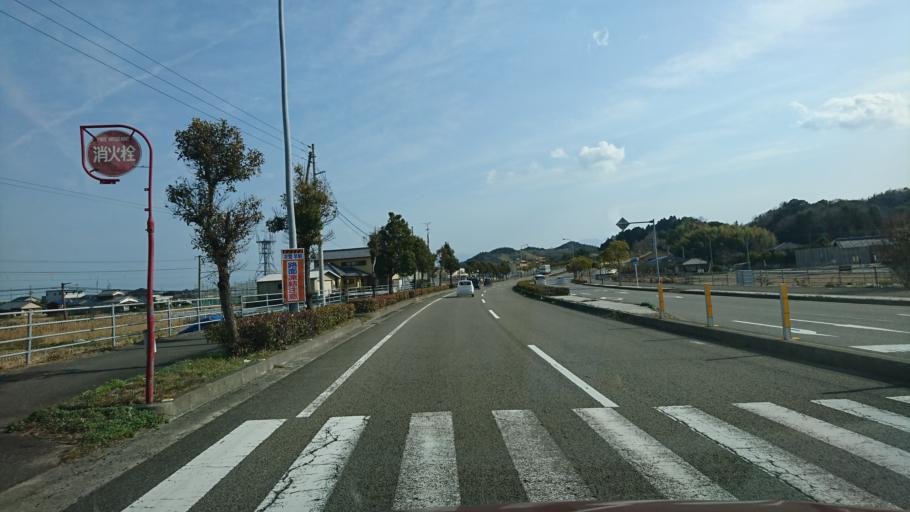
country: JP
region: Ehime
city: Saijo
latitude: 34.0188
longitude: 133.0289
